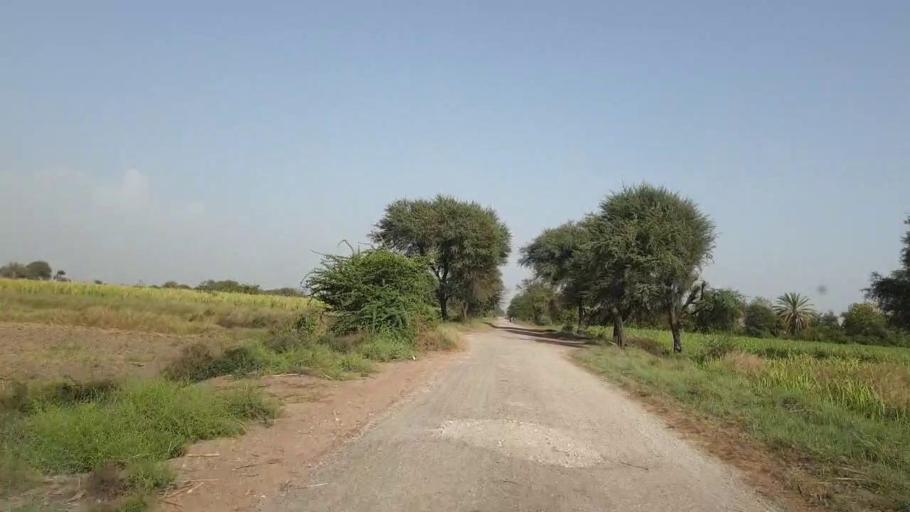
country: PK
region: Sindh
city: Tando Ghulam Ali
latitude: 25.0762
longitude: 68.8425
